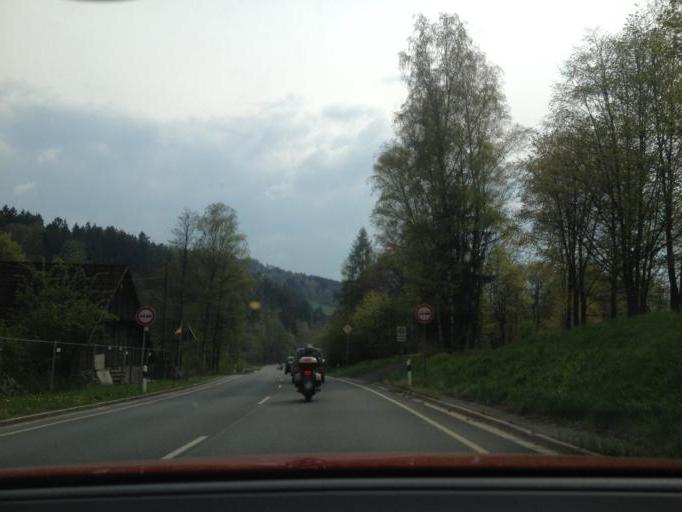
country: DE
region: Bavaria
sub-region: Upper Franconia
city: Goldkronach
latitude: 50.0327
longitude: 11.7084
